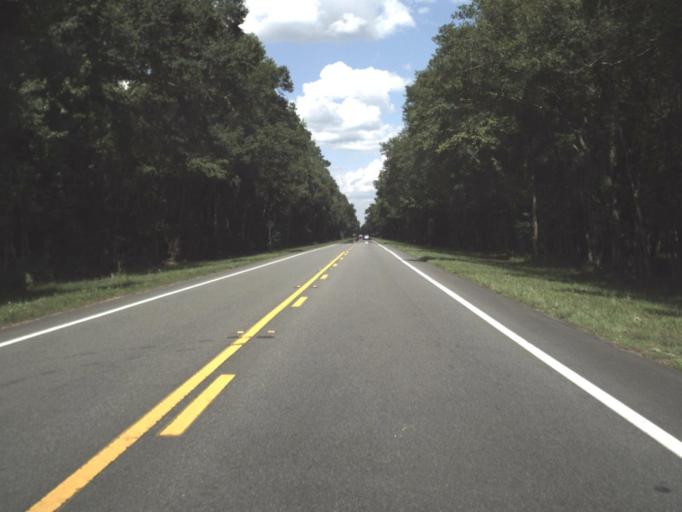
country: US
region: Florida
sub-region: Alachua County
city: Gainesville
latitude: 29.6879
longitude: -82.2371
